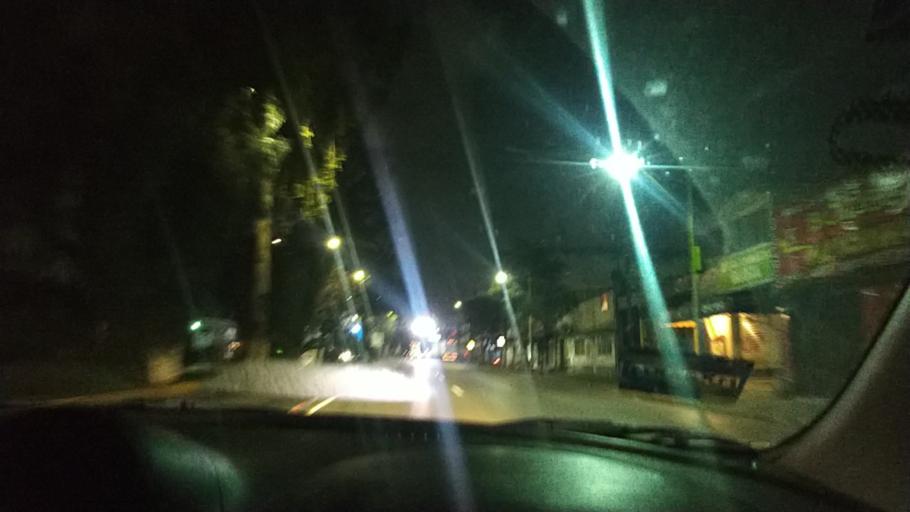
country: MX
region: Mexico
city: Ecatepec
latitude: 19.6121
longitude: -99.0596
